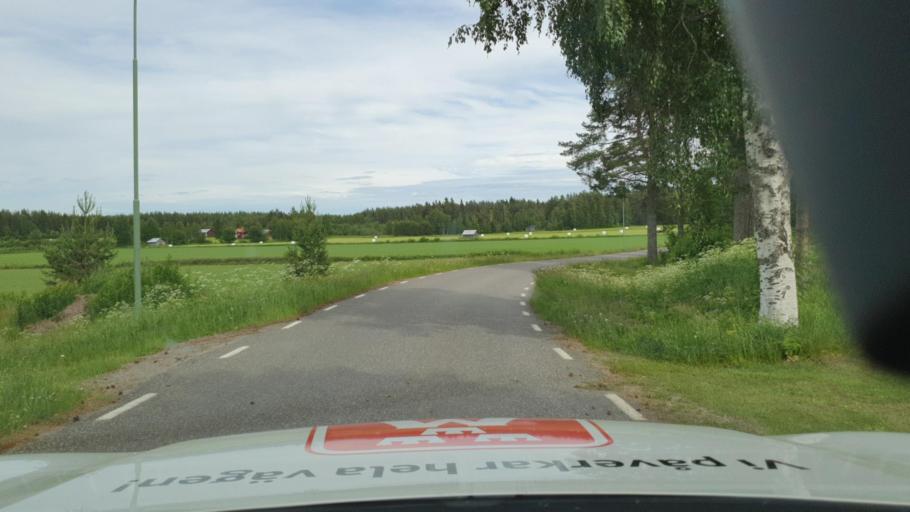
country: SE
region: Vaesterbotten
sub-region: Skelleftea Kommun
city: Burtraesk
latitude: 64.4974
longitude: 20.8658
